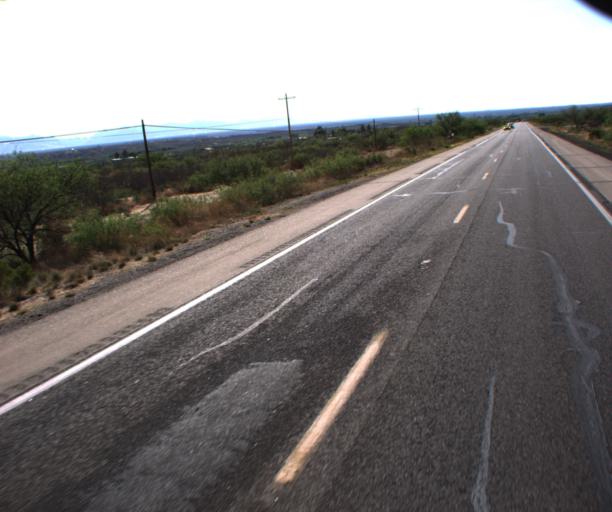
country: US
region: Arizona
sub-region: Cochise County
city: Benson
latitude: 31.9248
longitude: -110.2738
